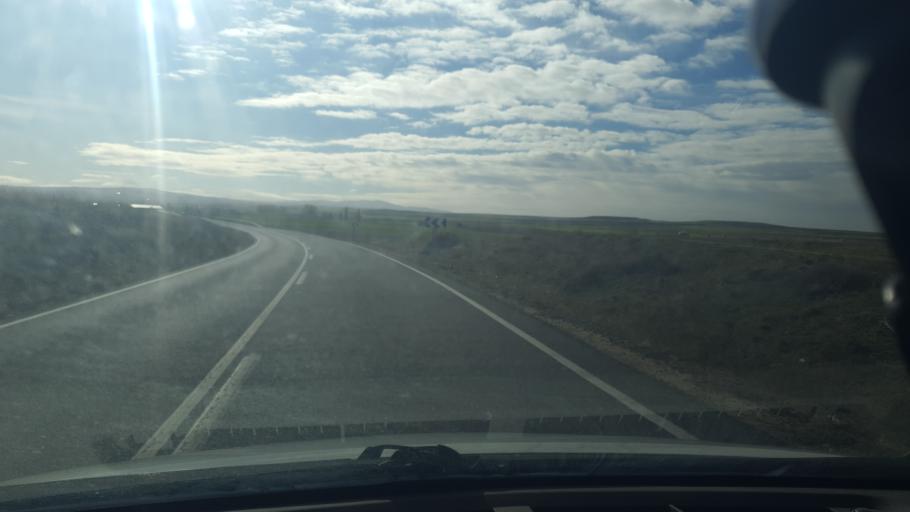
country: ES
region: Castille and Leon
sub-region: Provincia de Avila
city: Gotarrendura
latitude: 40.8186
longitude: -4.7498
